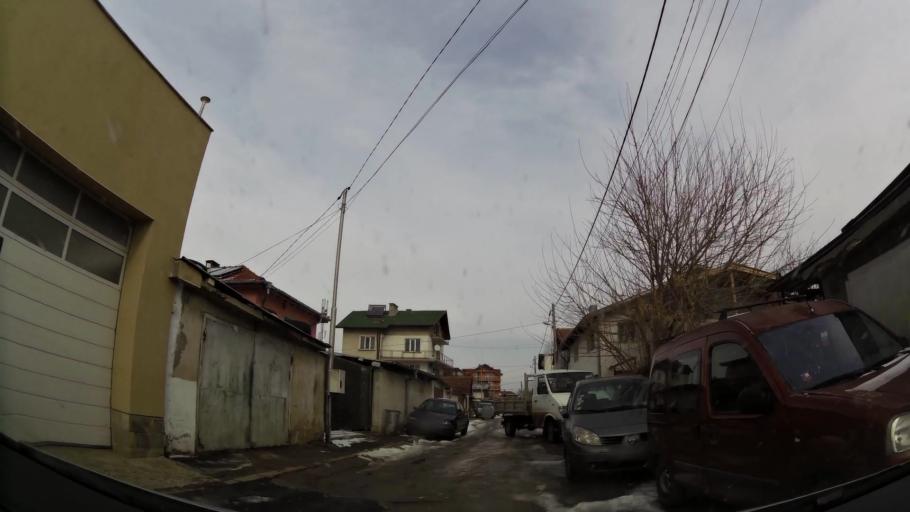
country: BG
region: Sofia-Capital
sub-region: Stolichna Obshtina
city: Sofia
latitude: 42.7124
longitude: 23.4167
